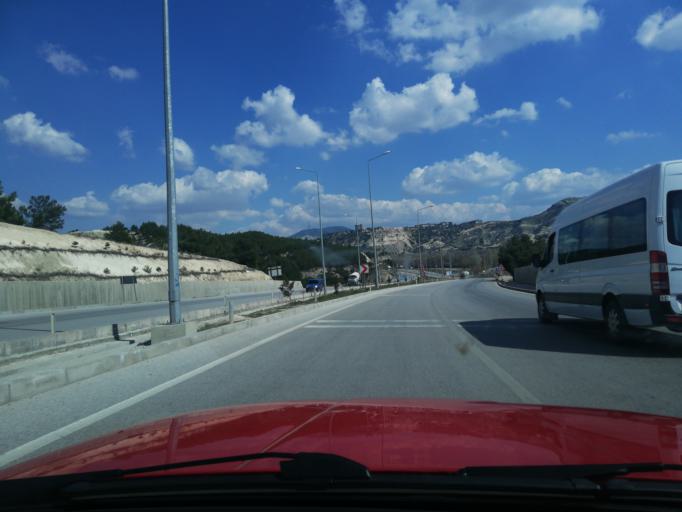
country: TR
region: Burdur
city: Burdur
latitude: 37.7007
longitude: 30.3177
